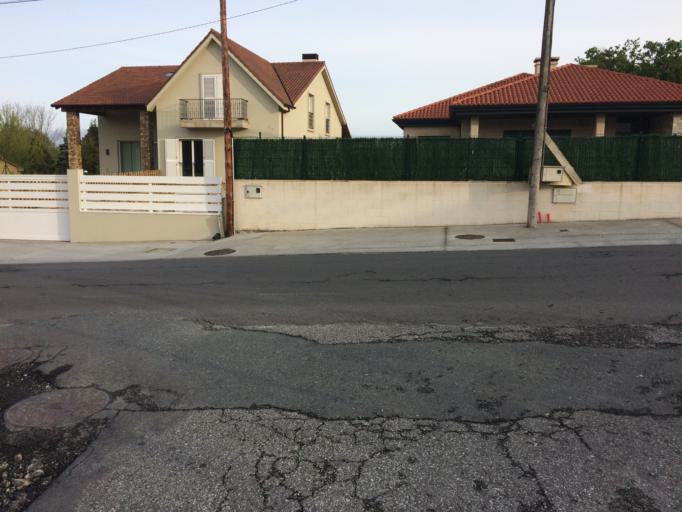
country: ES
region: Galicia
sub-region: Provincia da Coruna
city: Ames
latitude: 42.8331
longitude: -8.6049
